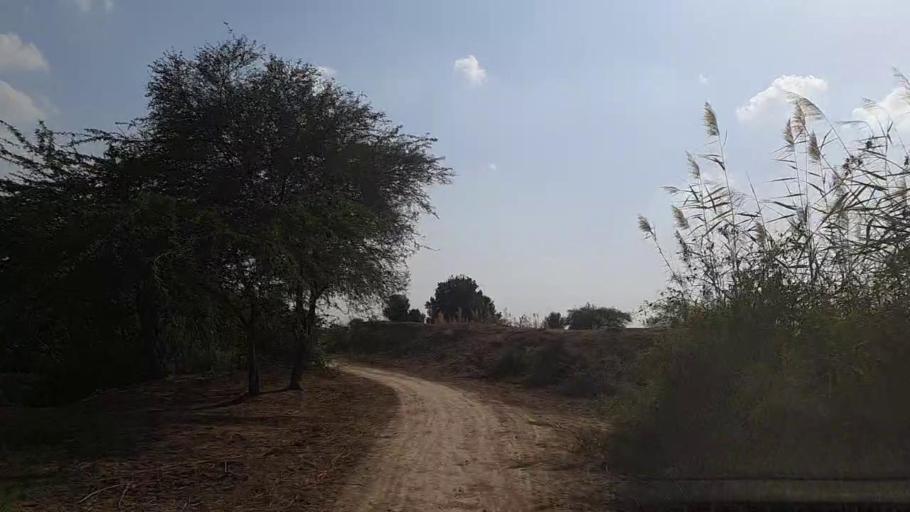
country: PK
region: Sindh
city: Jati
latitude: 24.4756
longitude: 68.3379
